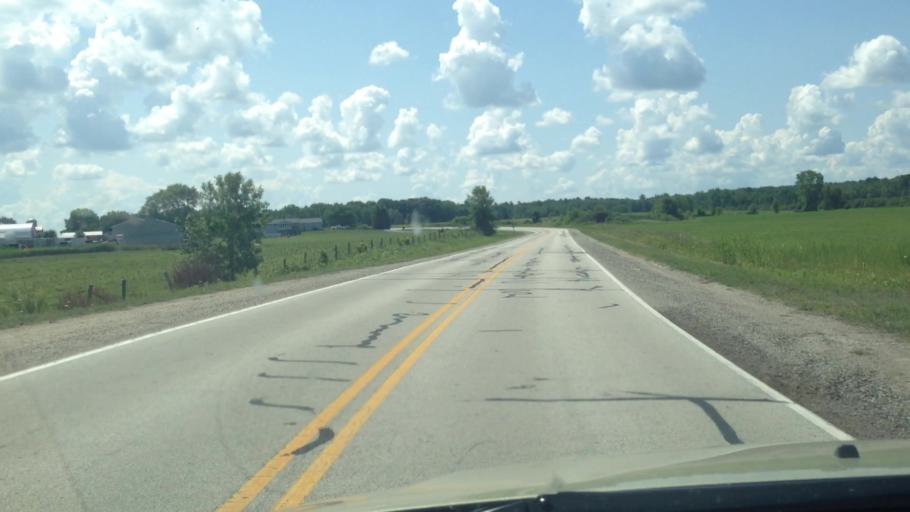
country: US
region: Wisconsin
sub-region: Brown County
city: Suamico
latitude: 44.6599
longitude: -88.0528
